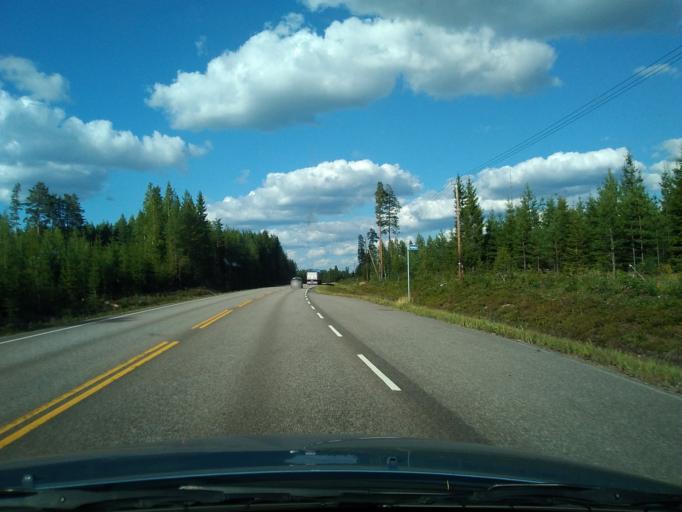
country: FI
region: Pirkanmaa
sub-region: Ylae-Pirkanmaa
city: Maenttae
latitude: 62.1123
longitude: 24.7406
